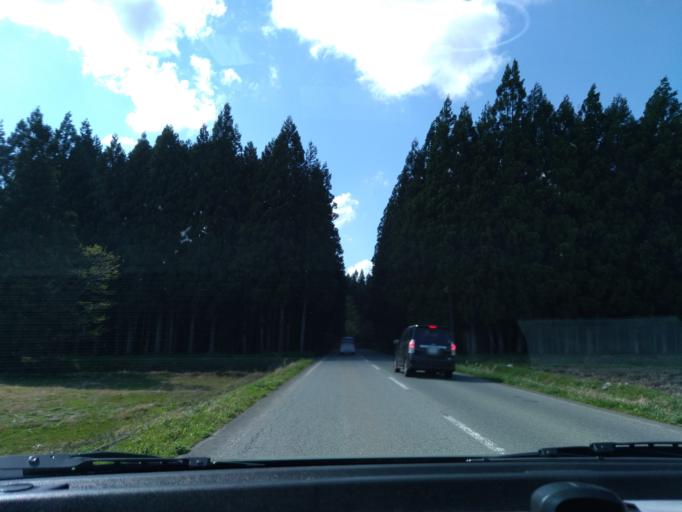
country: JP
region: Akita
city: Akita
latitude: 39.6888
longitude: 140.2767
